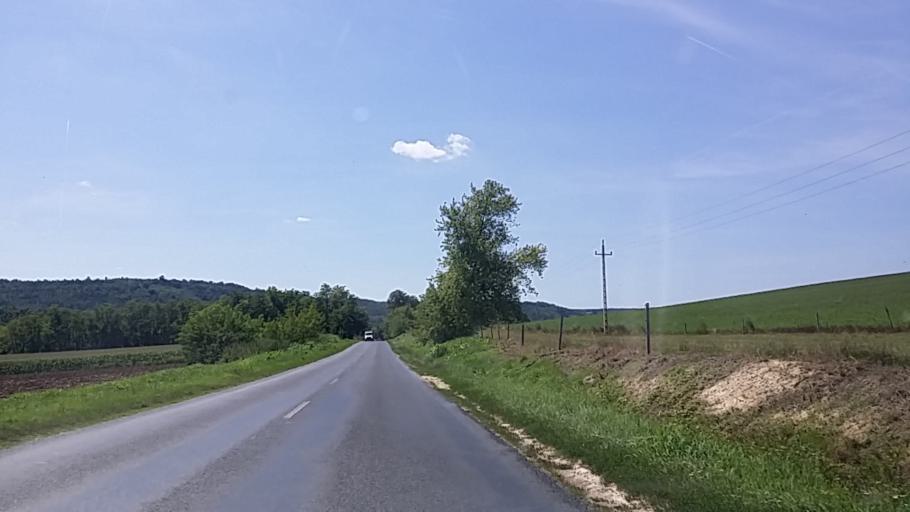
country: HU
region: Somogy
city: Tab
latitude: 46.7190
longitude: 18.0095
